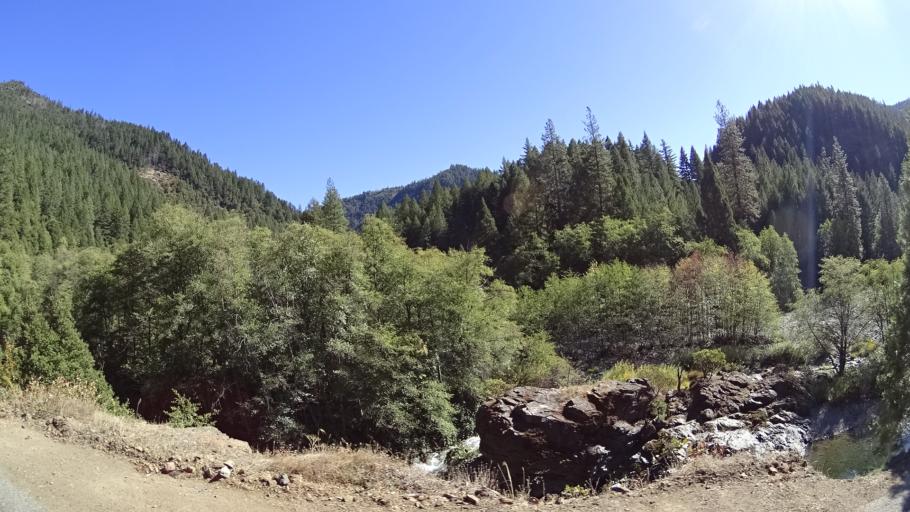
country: US
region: California
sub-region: Siskiyou County
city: Happy Camp
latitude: 41.2996
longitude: -123.1233
